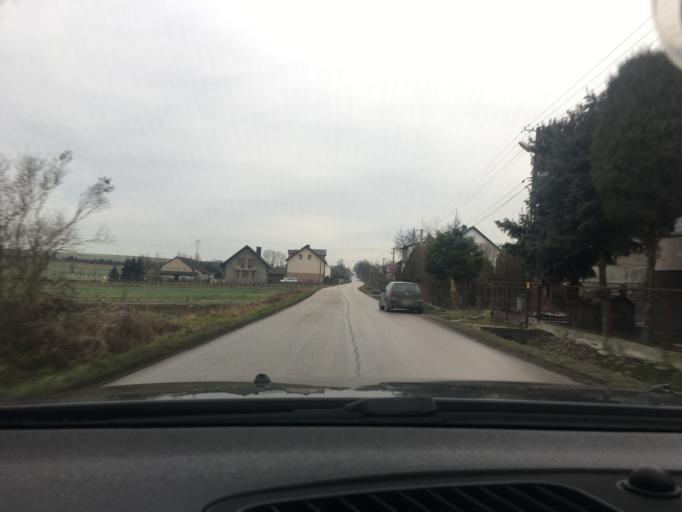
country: PL
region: Swietokrzyskie
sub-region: Powiat jedrzejowski
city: Jedrzejow
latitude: 50.6406
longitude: 20.3614
